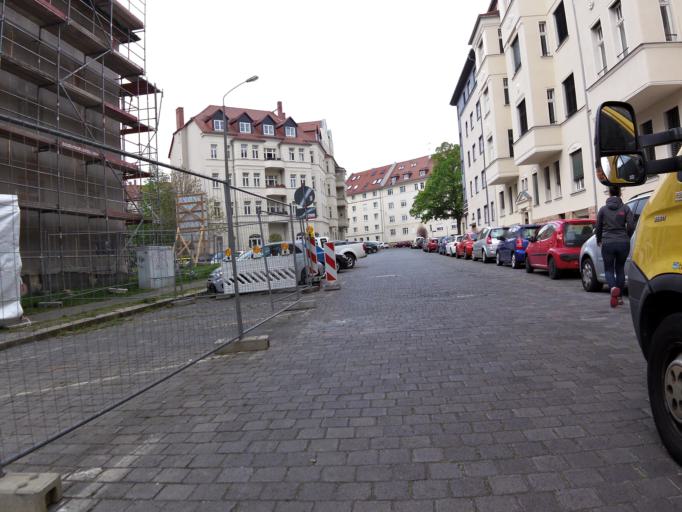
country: DE
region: Saxony
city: Leipzig
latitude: 51.3678
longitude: 12.3781
